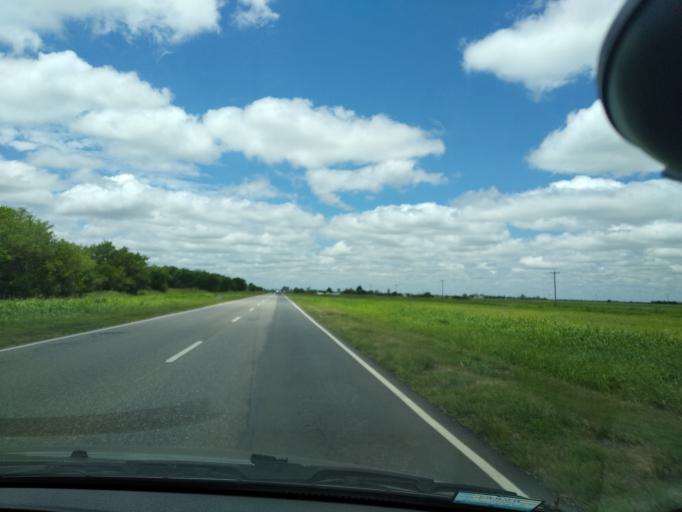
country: AR
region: Cordoba
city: Toledo
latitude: -31.6486
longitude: -64.1132
